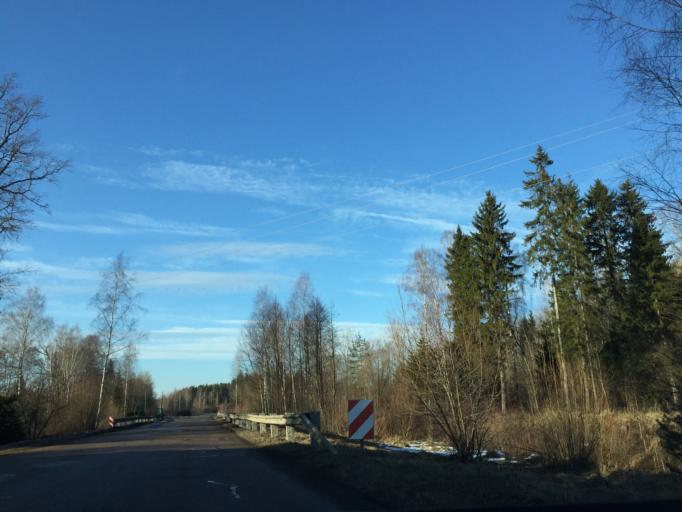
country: LV
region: Lecava
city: Iecava
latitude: 56.6924
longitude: 24.0890
